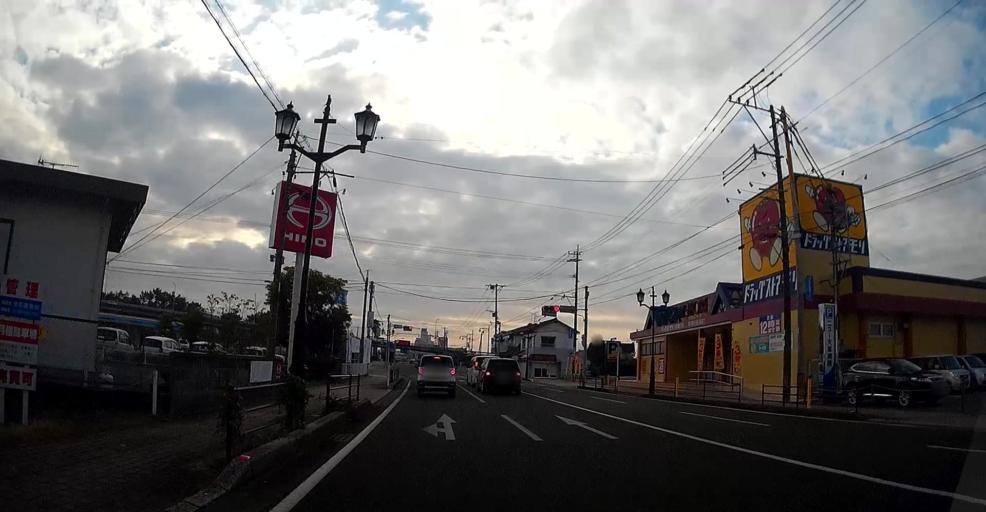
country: JP
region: Kumamoto
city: Hondo
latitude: 32.4484
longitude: 130.2000
